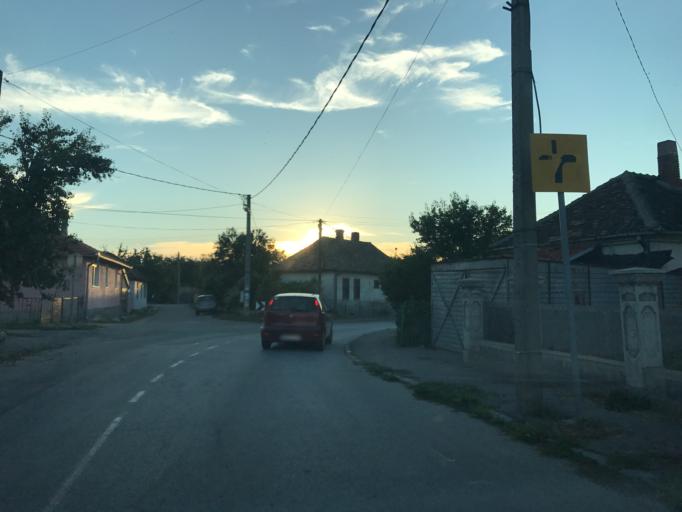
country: RS
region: Central Serbia
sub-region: Branicevski Okrug
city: Golubac
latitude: 44.6523
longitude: 21.6353
